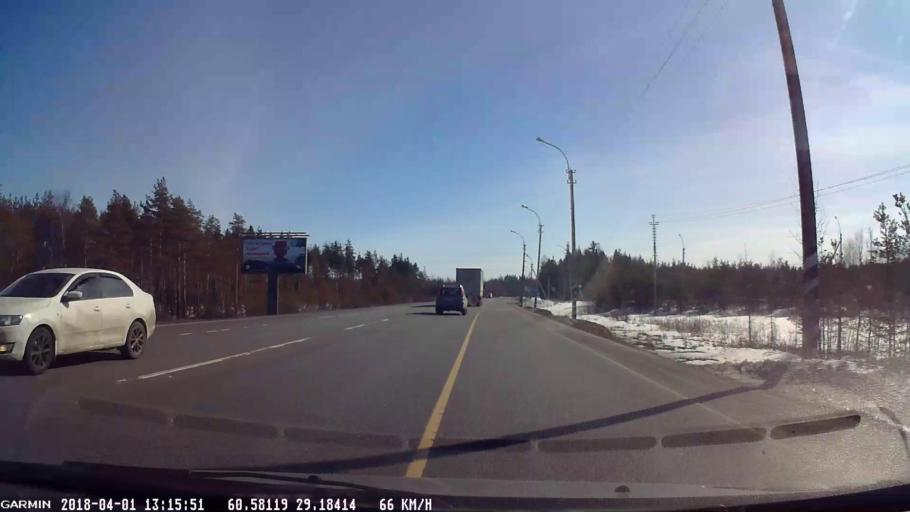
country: RU
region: Leningrad
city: Veshchevo
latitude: 60.5839
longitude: 29.1771
